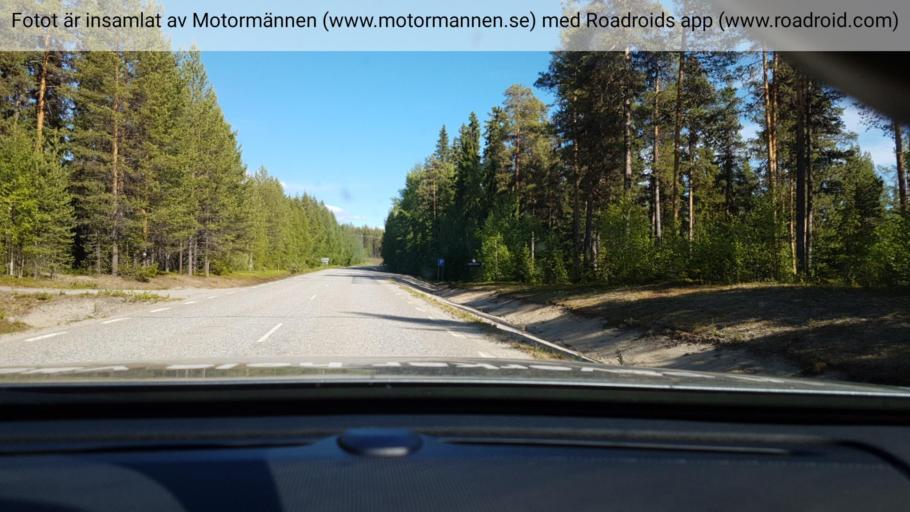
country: SE
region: Vaesterbotten
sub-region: Norsjo Kommun
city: Norsjoe
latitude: 64.6906
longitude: 19.2049
